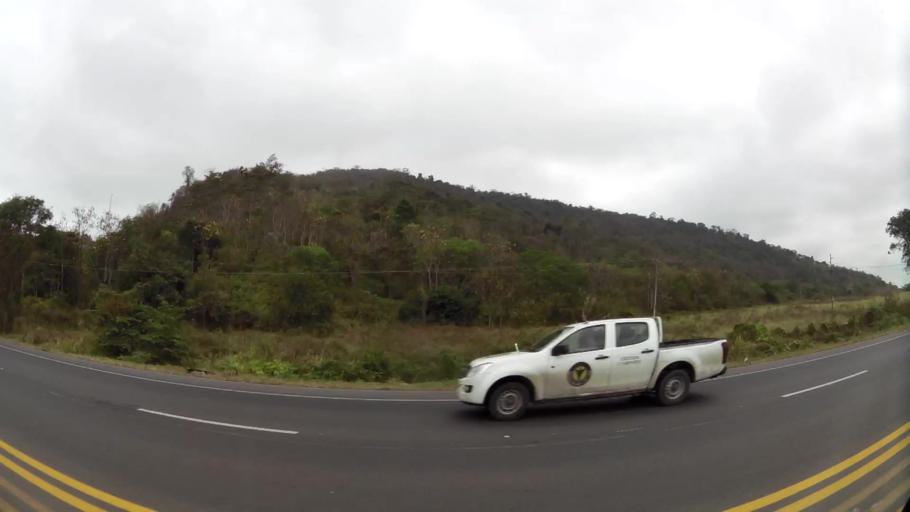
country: EC
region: Guayas
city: Naranjal
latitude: -2.4564
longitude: -79.6279
